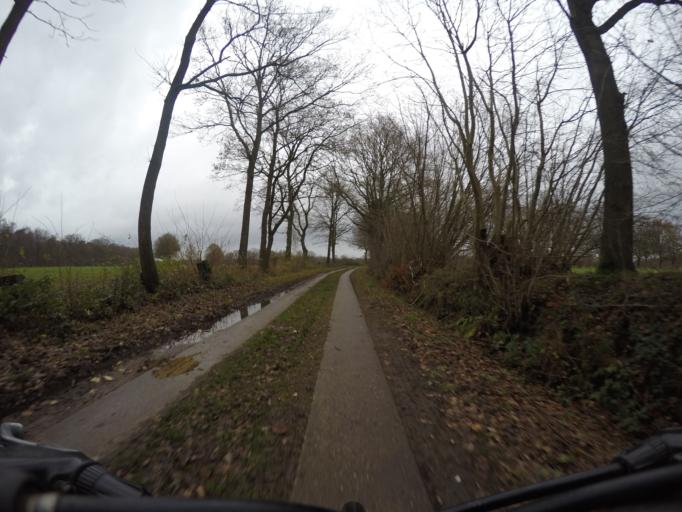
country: DE
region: Schleswig-Holstein
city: Borstel-Hohenraden
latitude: 53.7221
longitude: 9.8318
